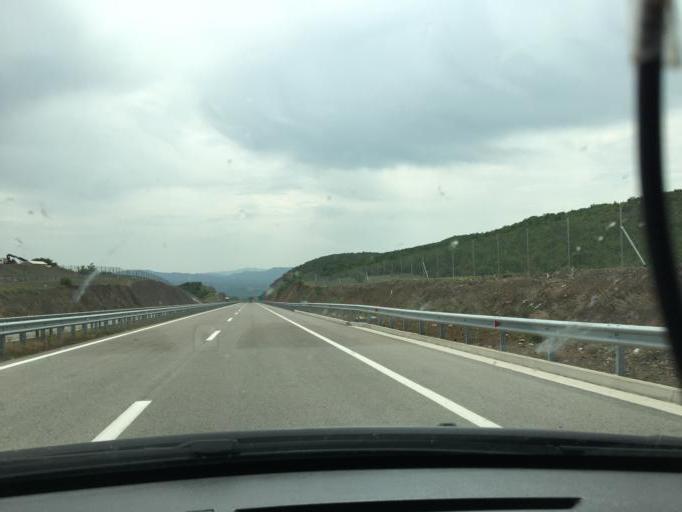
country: MK
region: Gevgelija
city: Miravci
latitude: 41.3146
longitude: 22.4142
